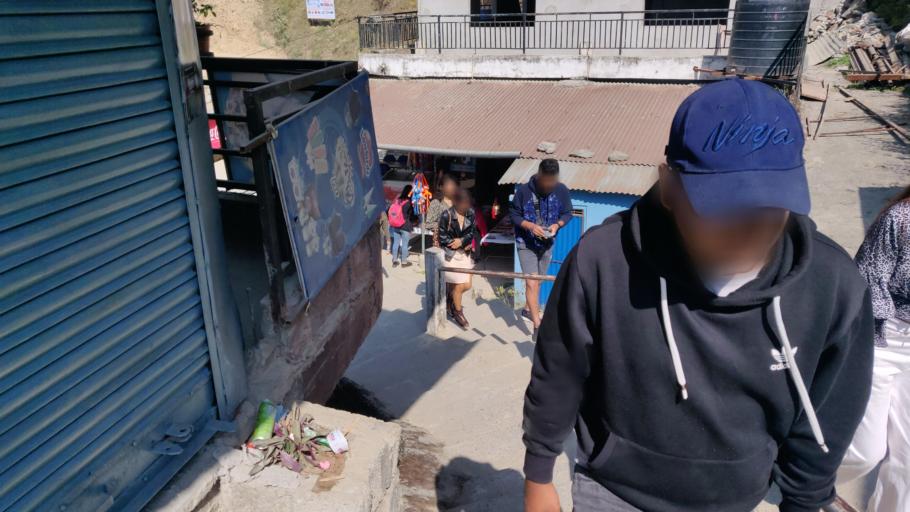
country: NP
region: Western Region
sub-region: Gandaki Zone
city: Pokhara
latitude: 28.2002
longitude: 83.9446
